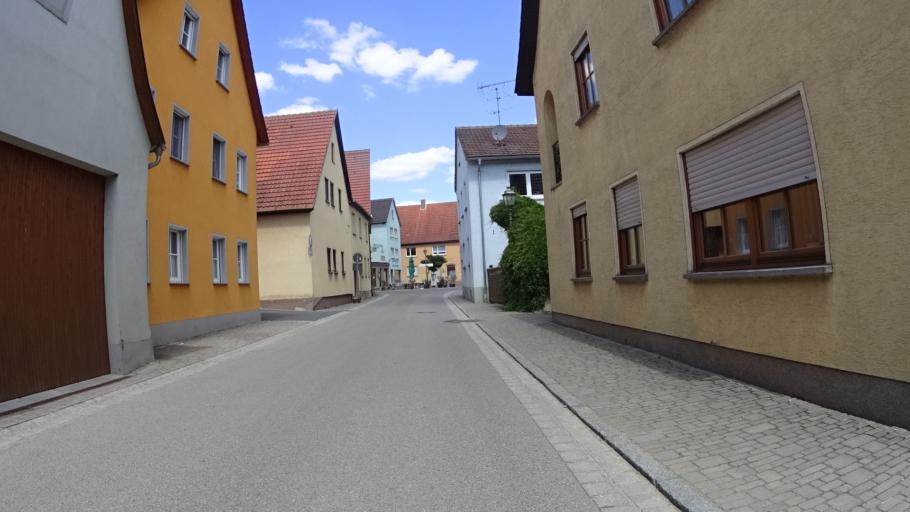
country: DE
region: Bavaria
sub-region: Regierungsbezirk Unterfranken
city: Rottingen
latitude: 49.5098
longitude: 9.9700
